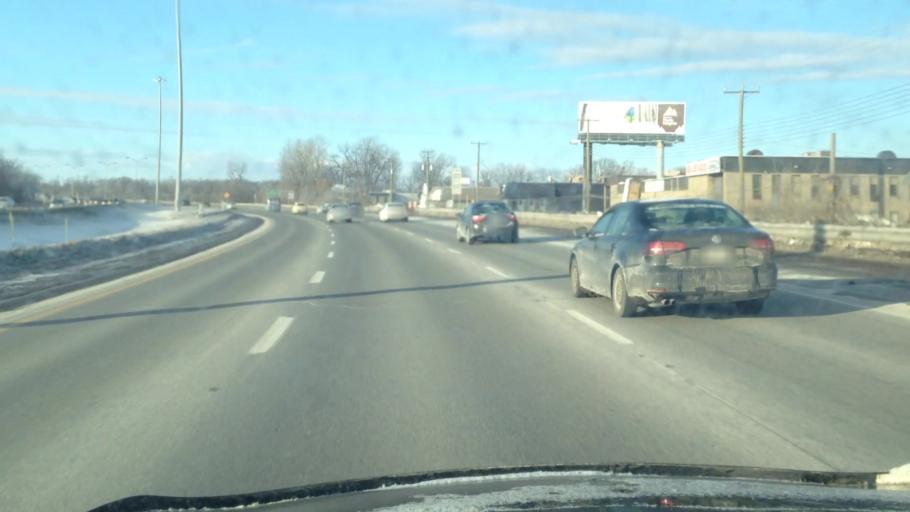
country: CA
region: Quebec
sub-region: Laurentides
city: Boisbriand
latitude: 45.6040
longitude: -73.8055
